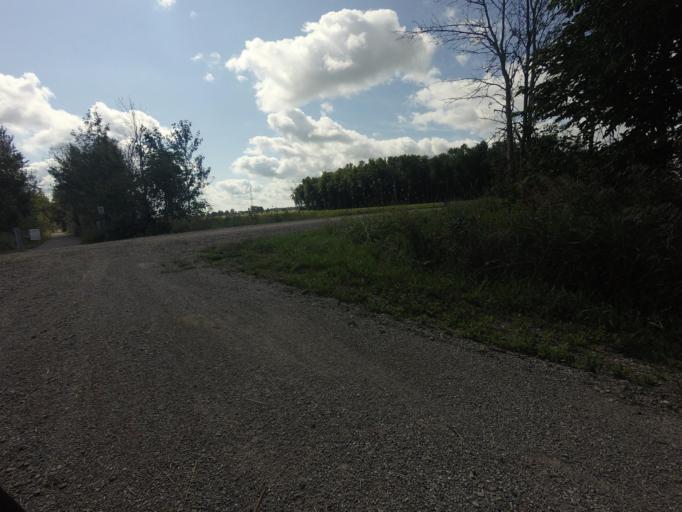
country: CA
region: Ontario
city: Huron East
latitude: 43.6985
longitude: -81.3439
